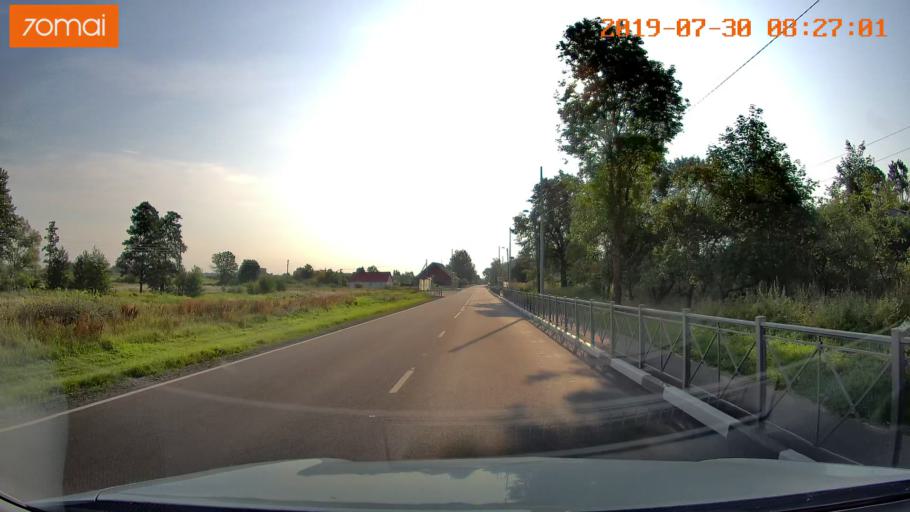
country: RU
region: Kaliningrad
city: Chernyakhovsk
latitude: 54.6265
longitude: 21.6165
